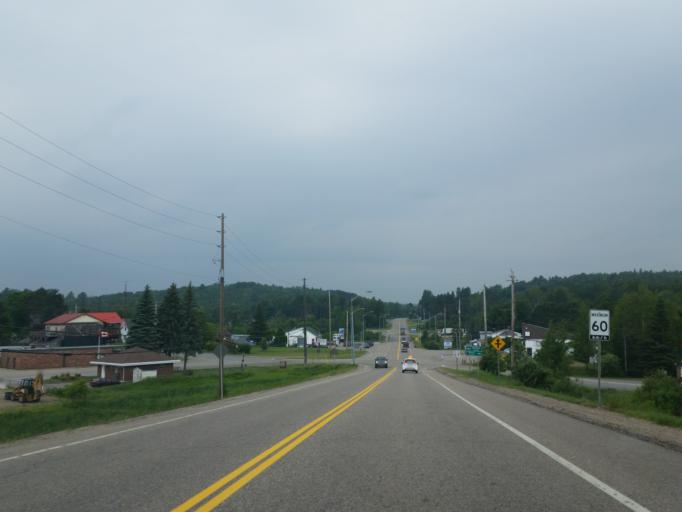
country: CA
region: Ontario
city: Bancroft
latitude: 45.4919
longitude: -78.2363
